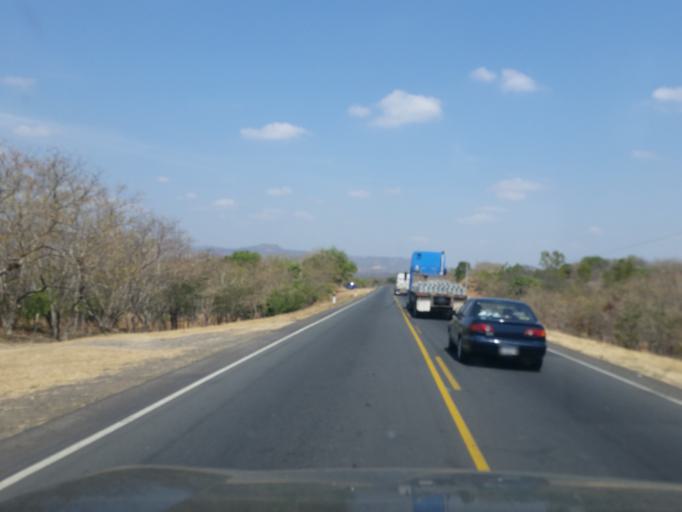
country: NI
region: Matagalpa
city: Ciudad Dario
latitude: 12.6334
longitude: -86.0578
